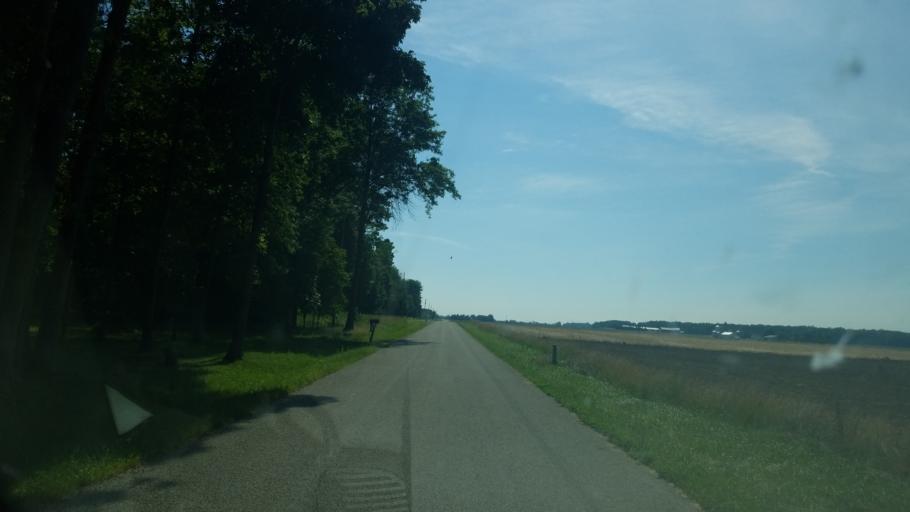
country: US
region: Ohio
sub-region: Wyandot County
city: Carey
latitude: 41.0142
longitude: -83.3499
